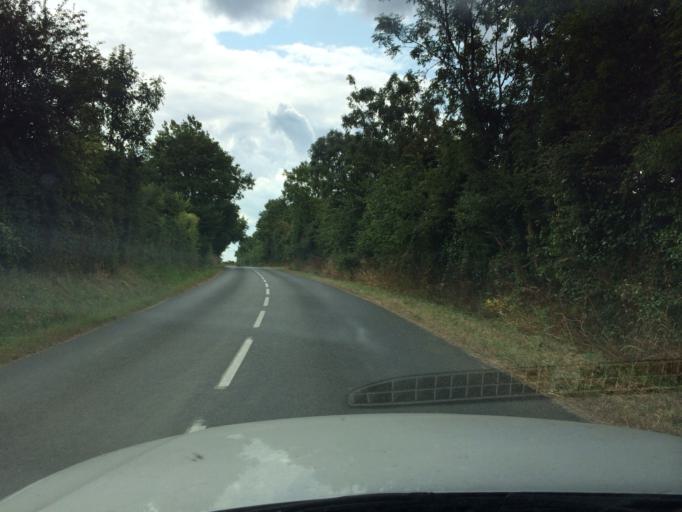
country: FR
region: Lower Normandy
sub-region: Departement de la Manche
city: Sainte-Mere-Eglise
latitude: 49.4539
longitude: -1.2682
